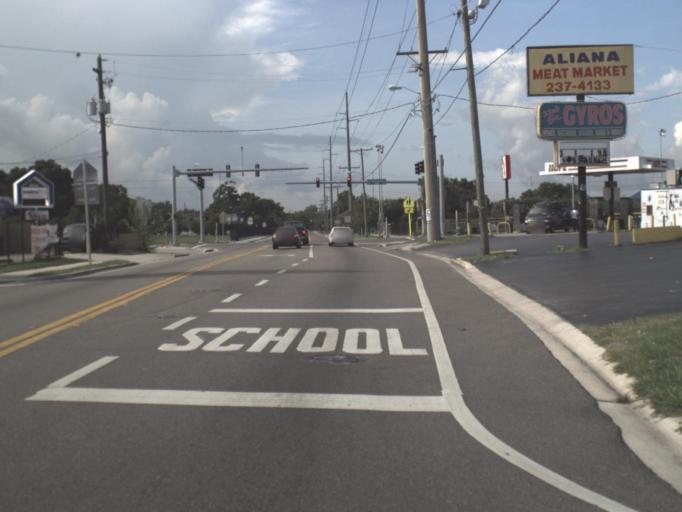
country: US
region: Florida
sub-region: Hillsborough County
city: Tampa
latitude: 27.9824
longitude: -82.4348
